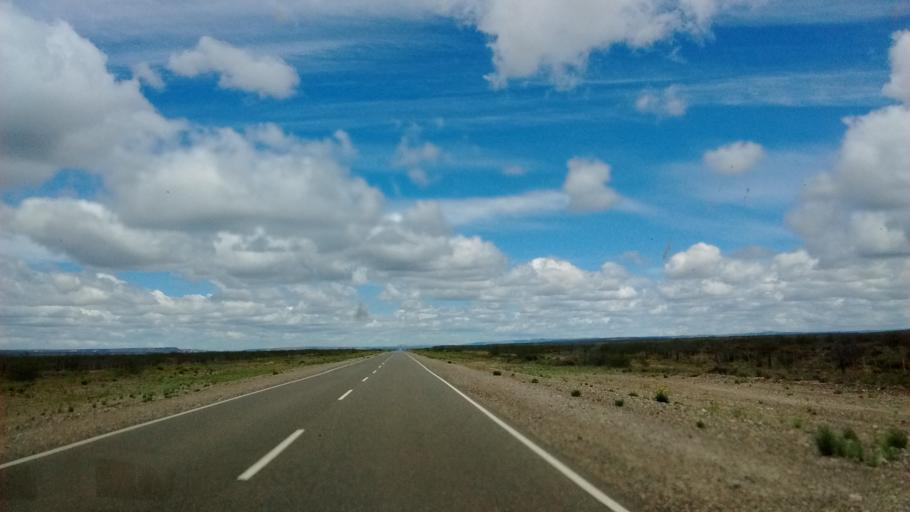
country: AR
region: Neuquen
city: Piedra del Aguila
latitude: -39.8180
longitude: -69.7301
